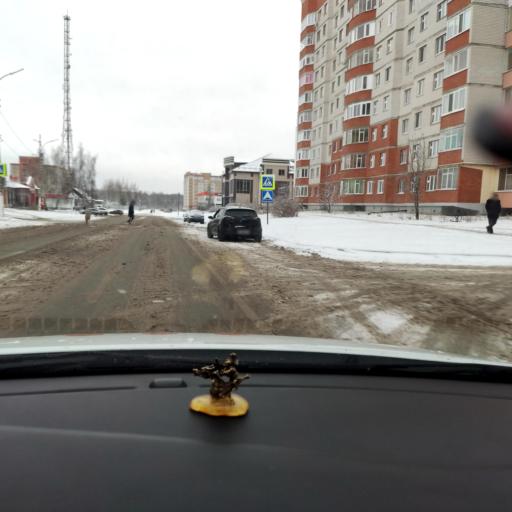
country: RU
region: Tatarstan
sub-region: Zelenodol'skiy Rayon
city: Zelenodolsk
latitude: 55.8591
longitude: 48.5667
